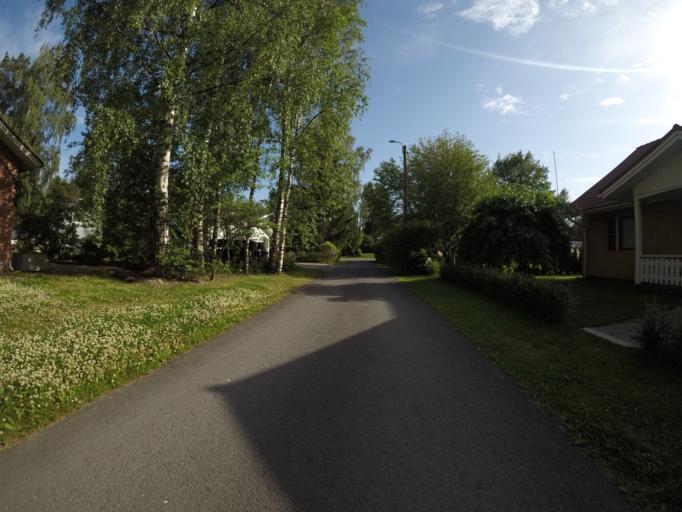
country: FI
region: Haeme
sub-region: Haemeenlinna
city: Haemeenlinna
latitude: 60.9814
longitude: 24.4165
